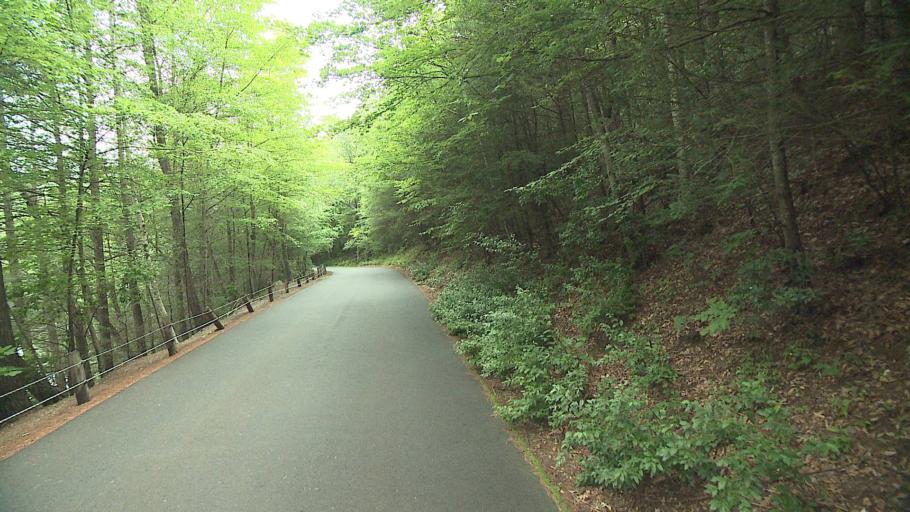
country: US
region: Connecticut
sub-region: Litchfield County
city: New Hartford Center
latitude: 41.9331
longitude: -72.9998
